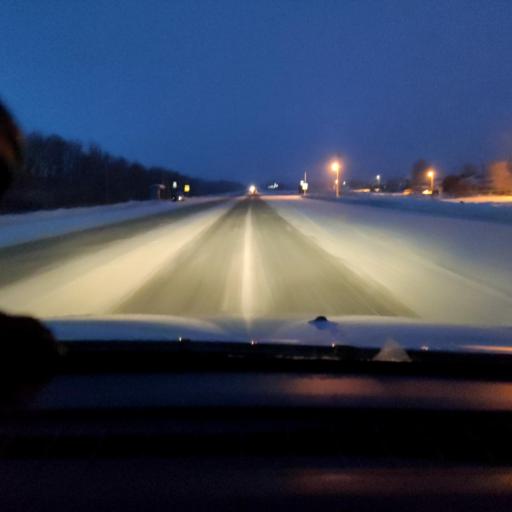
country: RU
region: Samara
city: Kinel'-Cherkassy
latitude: 53.4156
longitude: 51.4586
